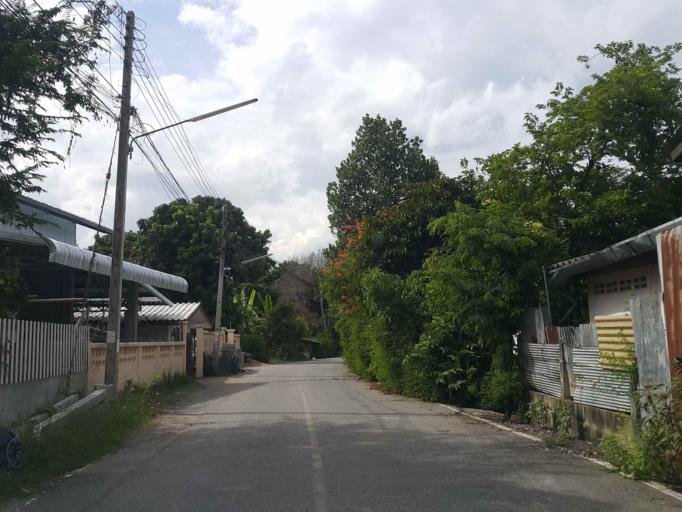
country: TH
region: Chiang Mai
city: Saraphi
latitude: 18.7379
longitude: 99.0567
